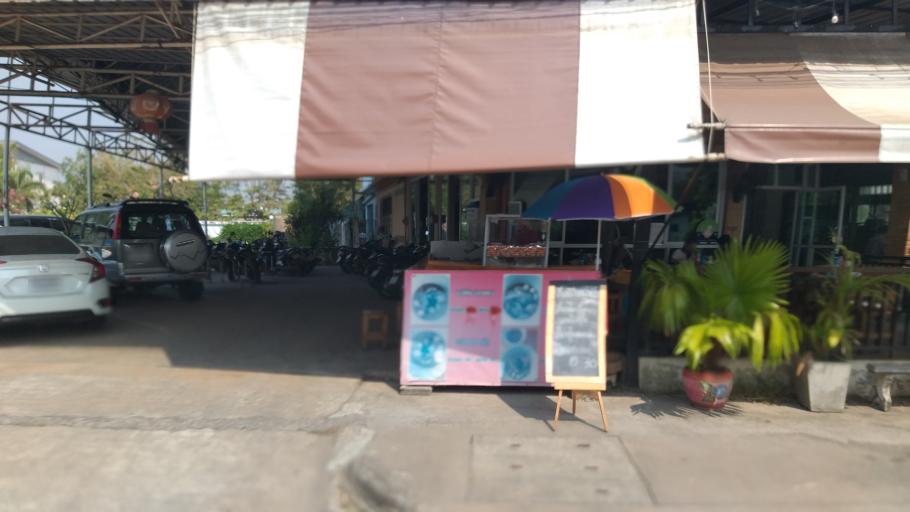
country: TH
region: Changwat Udon Thani
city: Udon Thani
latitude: 17.4161
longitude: 102.7735
